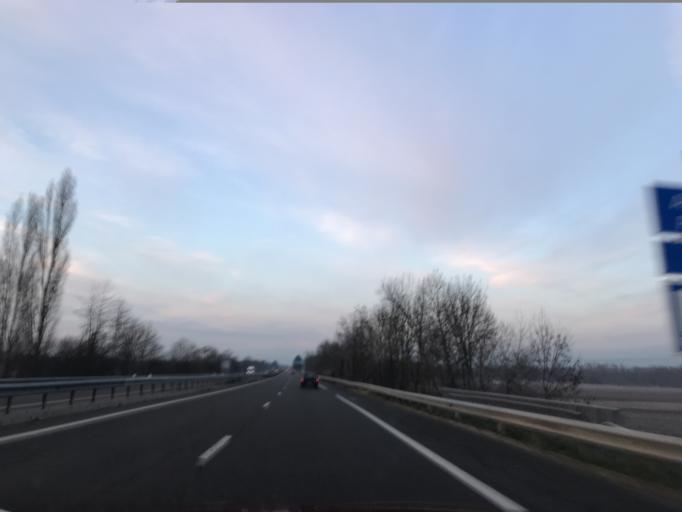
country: FR
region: Auvergne
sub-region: Departement du Puy-de-Dome
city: Culhat
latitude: 45.8378
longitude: 3.3051
